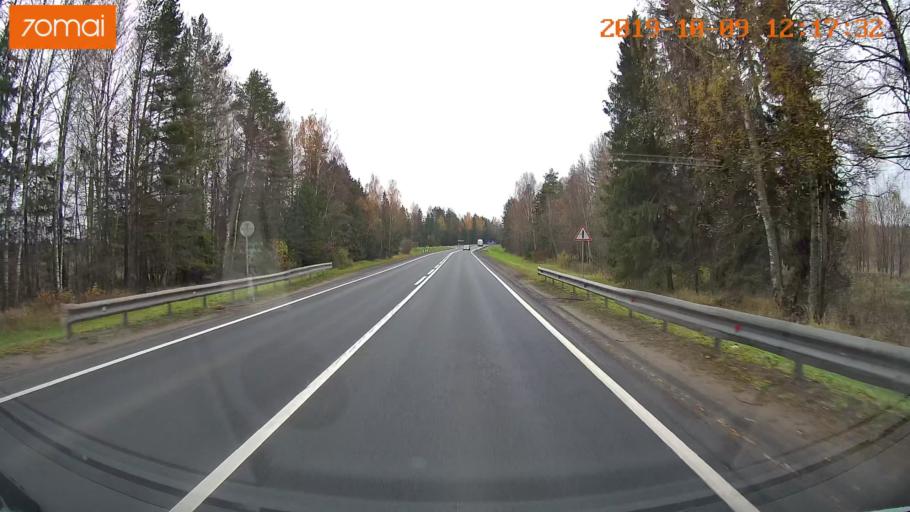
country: RU
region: Jaroslavl
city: Prechistoye
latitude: 58.4549
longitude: 40.3216
